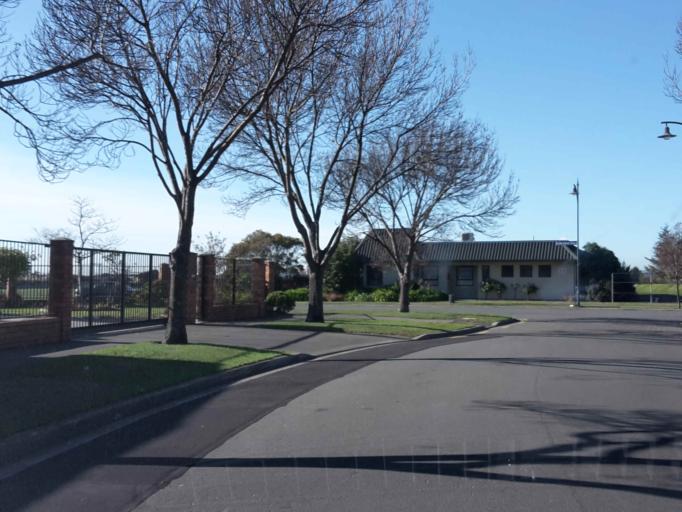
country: NZ
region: Canterbury
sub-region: Selwyn District
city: Prebbleton
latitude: -43.5446
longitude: 172.5471
